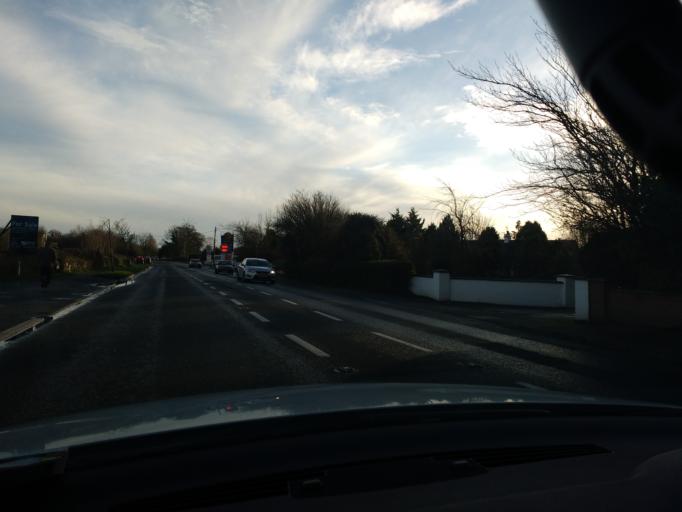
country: IE
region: Munster
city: Thurles
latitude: 52.6672
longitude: -7.8071
